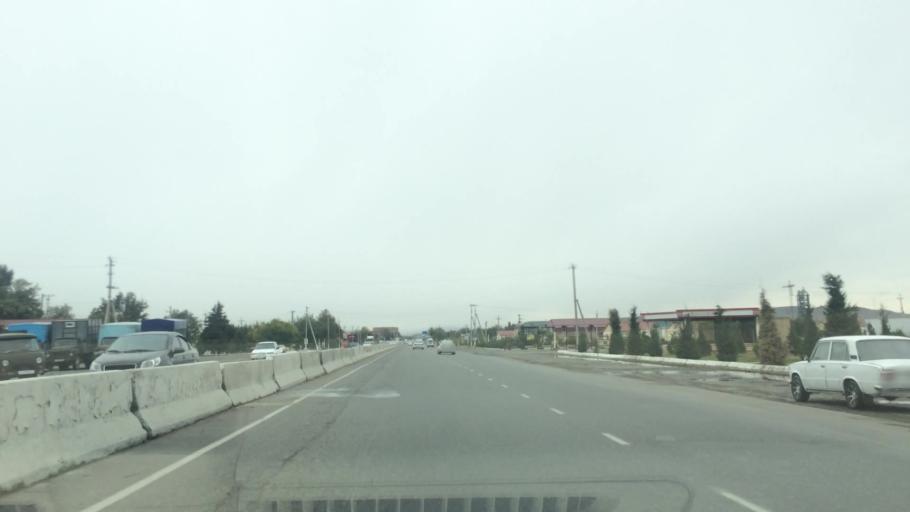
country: UZ
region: Samarqand
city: Jomboy
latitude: 39.7032
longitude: 67.0790
